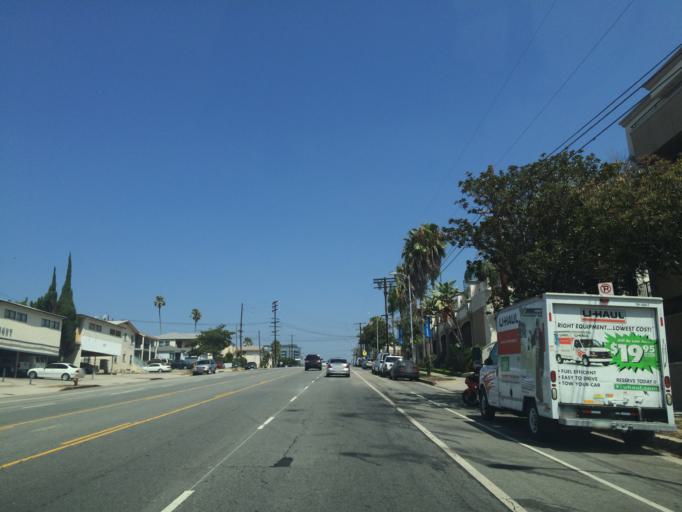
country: US
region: California
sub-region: Los Angeles County
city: Culver City
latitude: 34.0152
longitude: -118.4189
